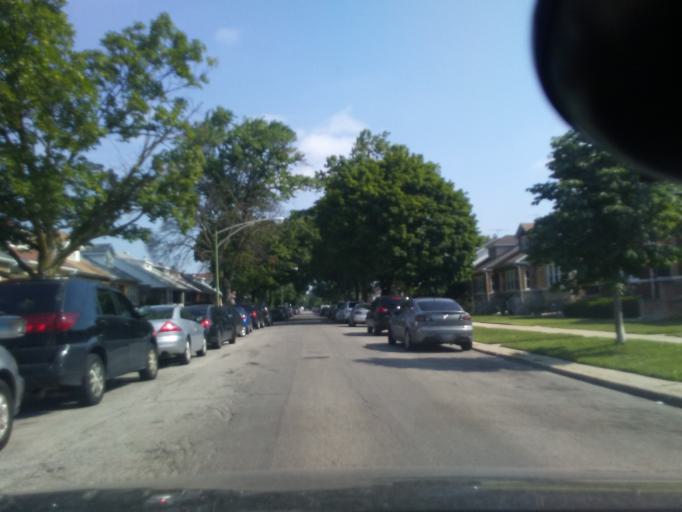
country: US
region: Illinois
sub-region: Cook County
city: Elmwood Park
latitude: 41.9278
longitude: -87.7686
